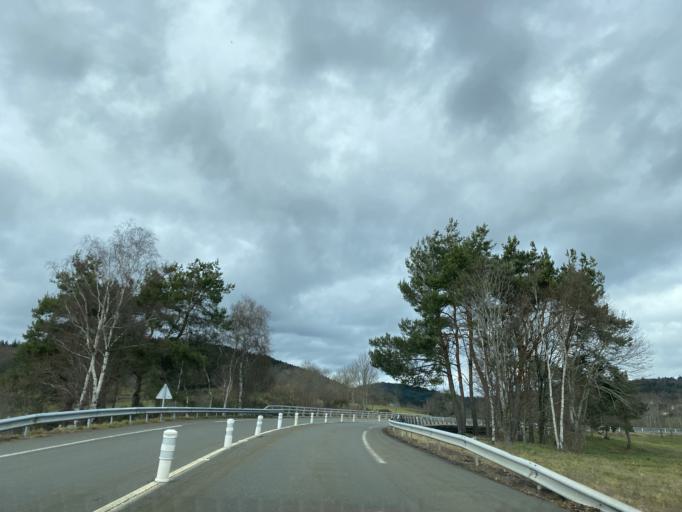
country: FR
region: Rhone-Alpes
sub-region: Departement de la Loire
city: Noiretable
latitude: 45.8528
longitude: 3.7912
